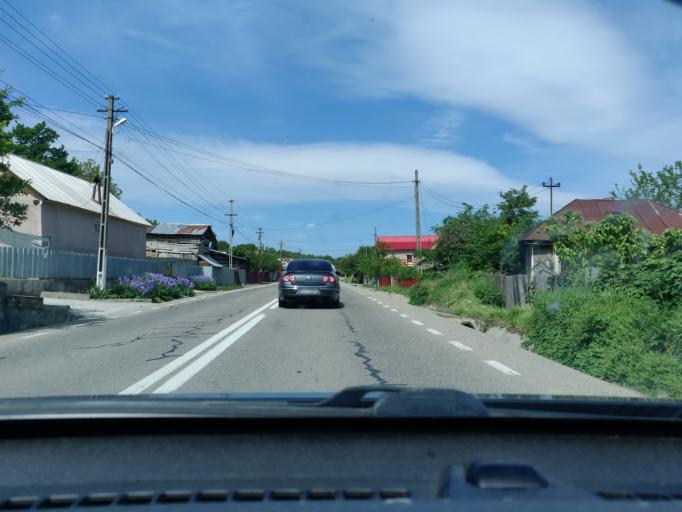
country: RO
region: Vrancea
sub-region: Comuna Vidra
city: Burca
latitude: 45.9058
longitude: 26.9663
